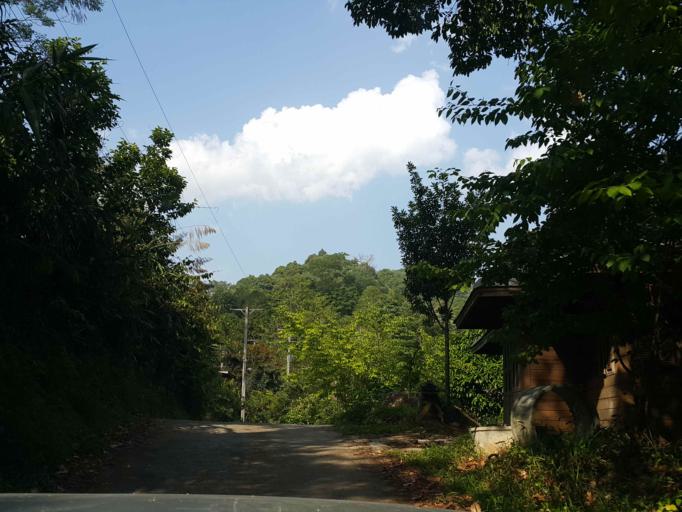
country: TH
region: Chiang Mai
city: Mae On
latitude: 18.9238
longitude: 99.3551
